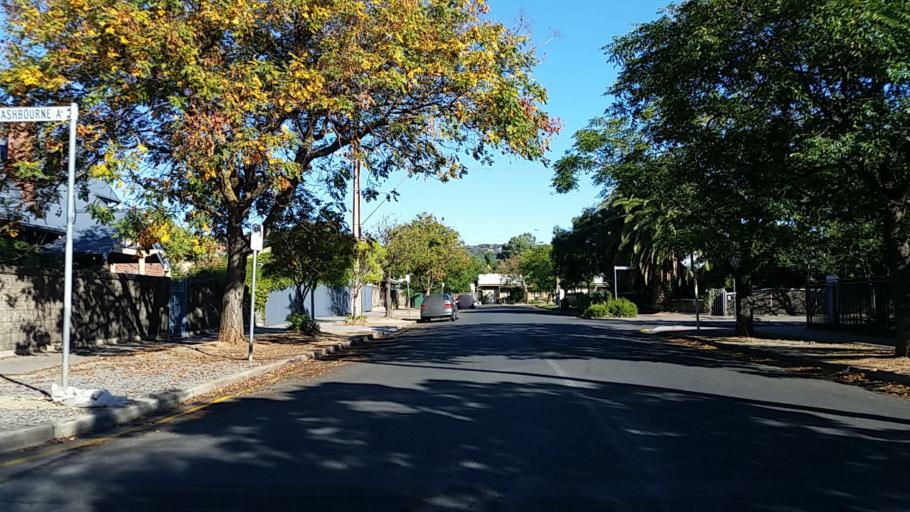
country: AU
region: South Australia
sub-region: Mitcham
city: Hawthorn
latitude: -34.9735
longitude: 138.6114
